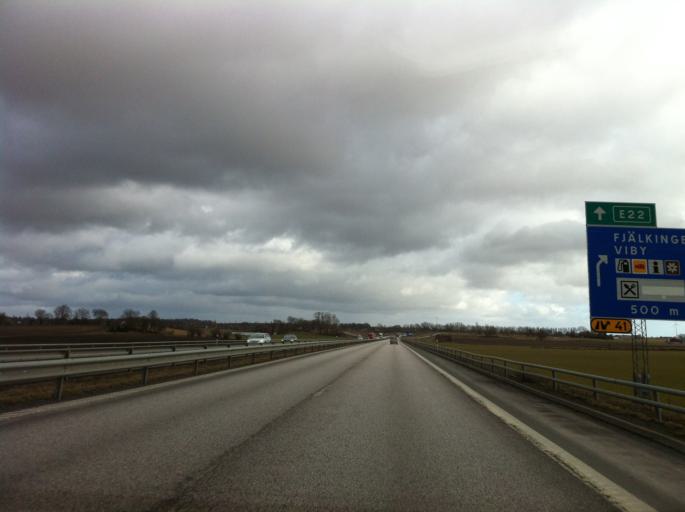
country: SE
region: Skane
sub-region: Kristianstads Kommun
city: Kristianstad
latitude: 56.0268
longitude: 14.0922
